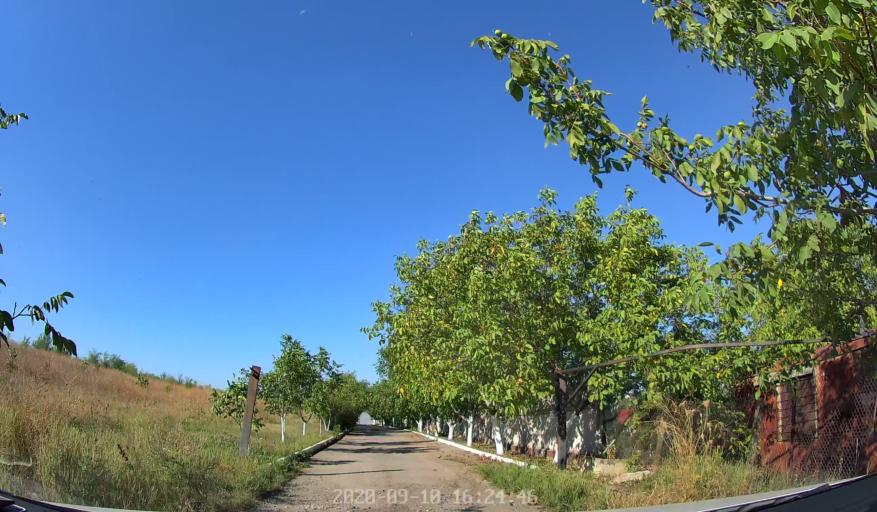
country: MD
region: Chisinau
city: Stauceni
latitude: 47.0540
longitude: 28.9206
